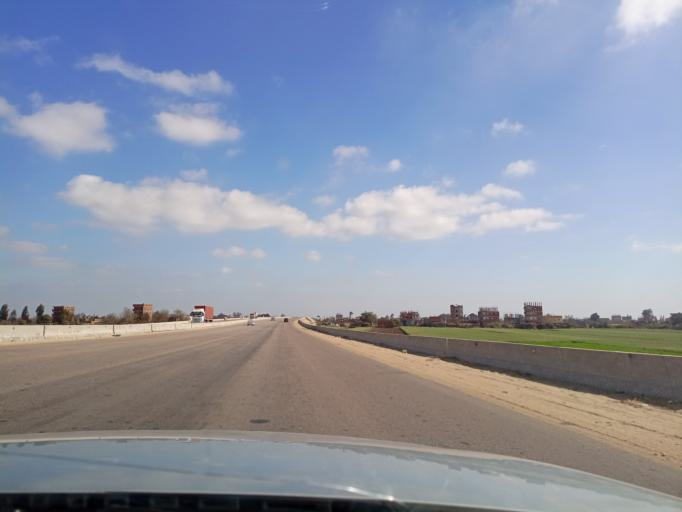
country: EG
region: Muhafazat al Minufiyah
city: Al Bajur
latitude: 30.3925
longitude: 30.9993
